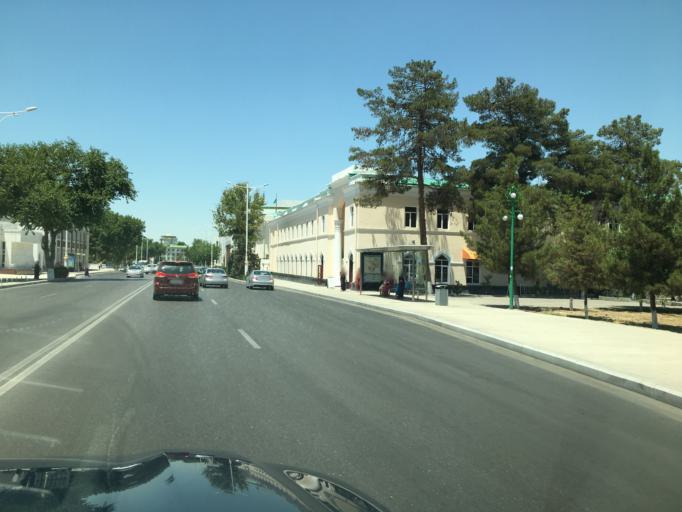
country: TM
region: Ahal
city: Ashgabat
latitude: 37.9398
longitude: 58.3803
